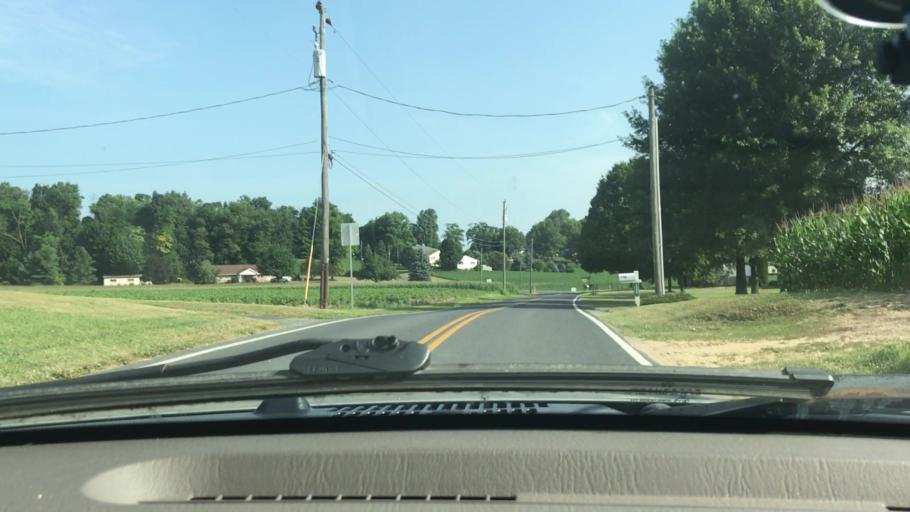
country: US
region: Pennsylvania
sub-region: Lancaster County
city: Rheems
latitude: 40.1502
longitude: -76.5717
